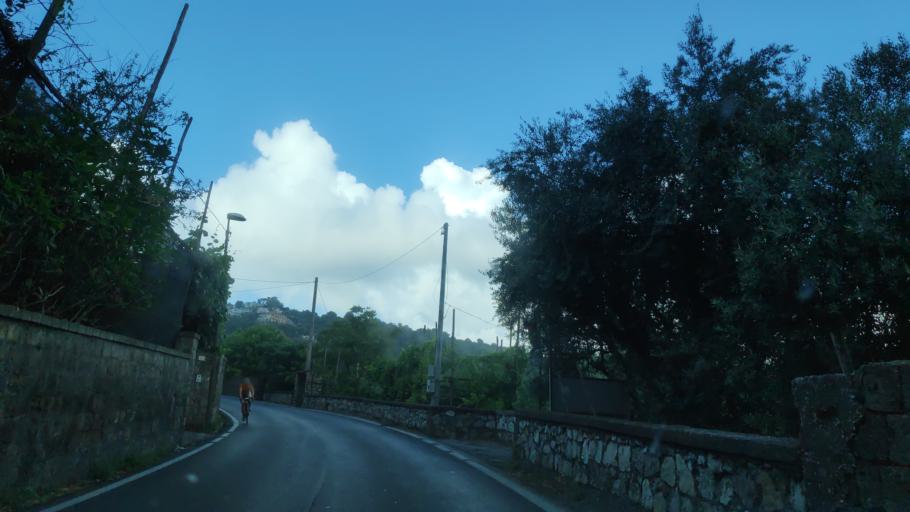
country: IT
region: Campania
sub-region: Provincia di Napoli
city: Piano di Sorrento
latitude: 40.6262
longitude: 14.4239
